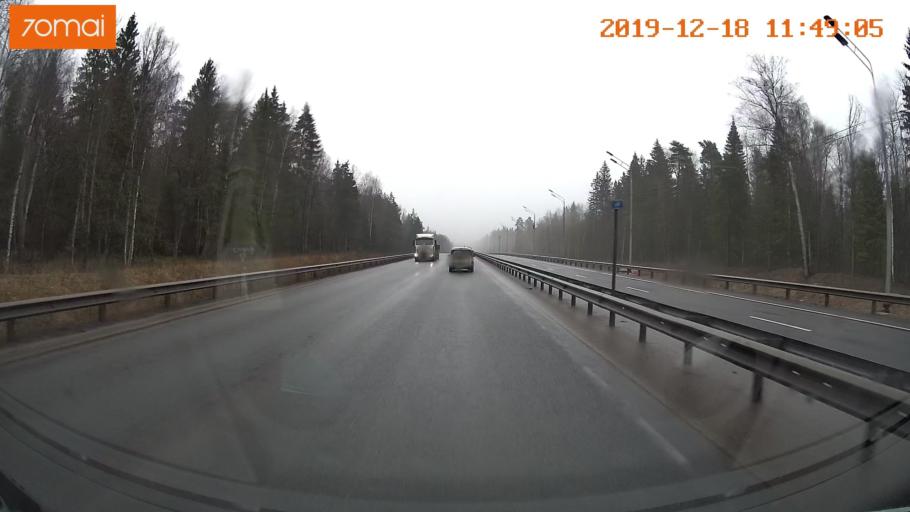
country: RU
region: Moskovskaya
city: Yershovo
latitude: 55.7744
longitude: 36.9089
